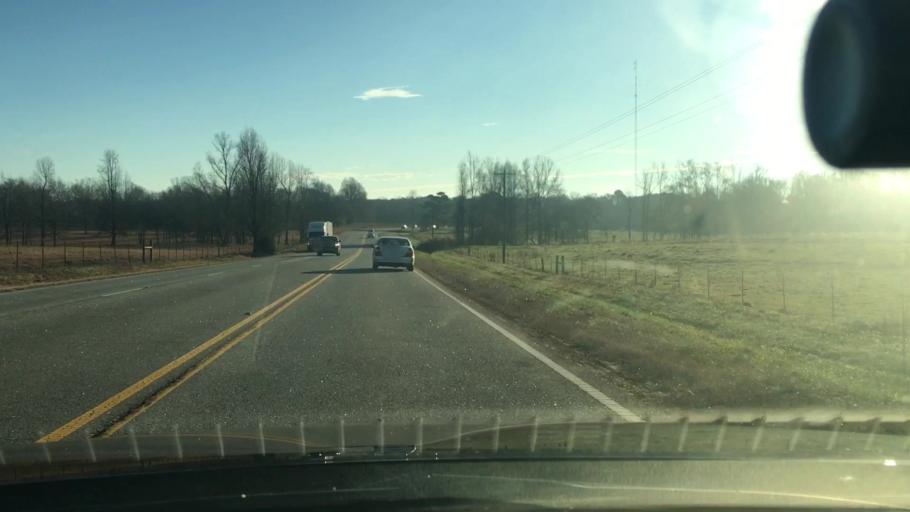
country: US
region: Georgia
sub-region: Coweta County
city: Senoia
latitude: 33.2464
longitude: -84.4358
